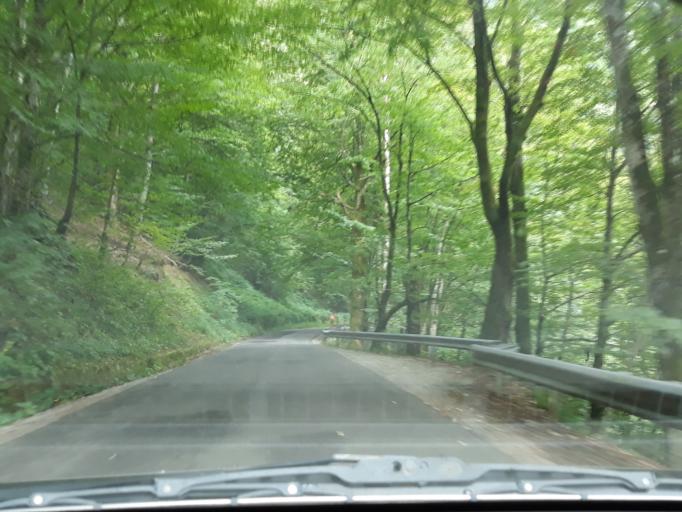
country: RO
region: Bihor
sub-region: Comuna Pietroasa
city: Pietroasa
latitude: 46.5871
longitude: 22.6267
